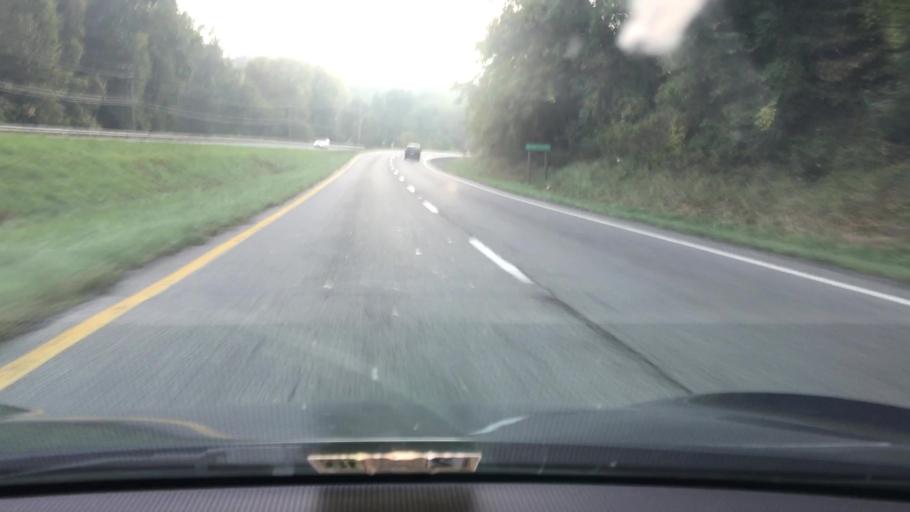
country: US
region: Virginia
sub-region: Botetourt County
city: Blue Ridge
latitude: 37.3973
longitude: -79.7538
